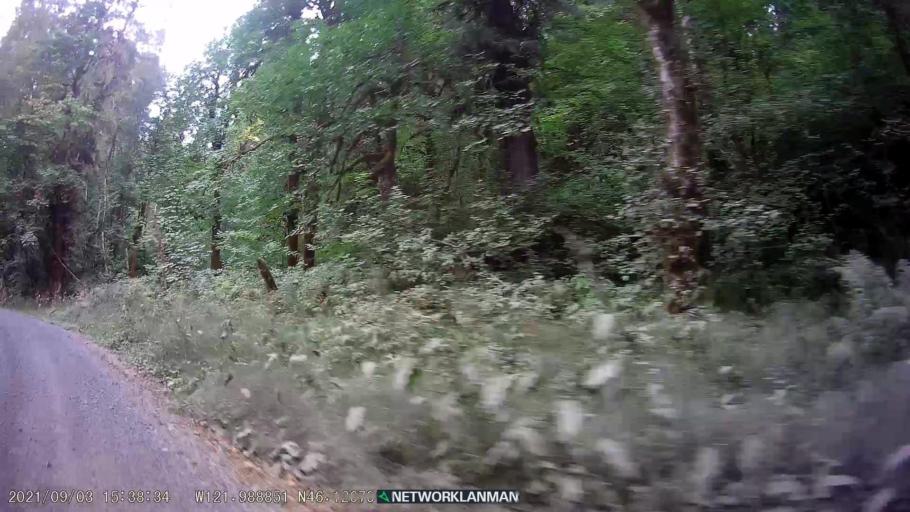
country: US
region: Washington
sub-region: Skamania County
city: Carson
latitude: 46.1268
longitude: -121.9885
